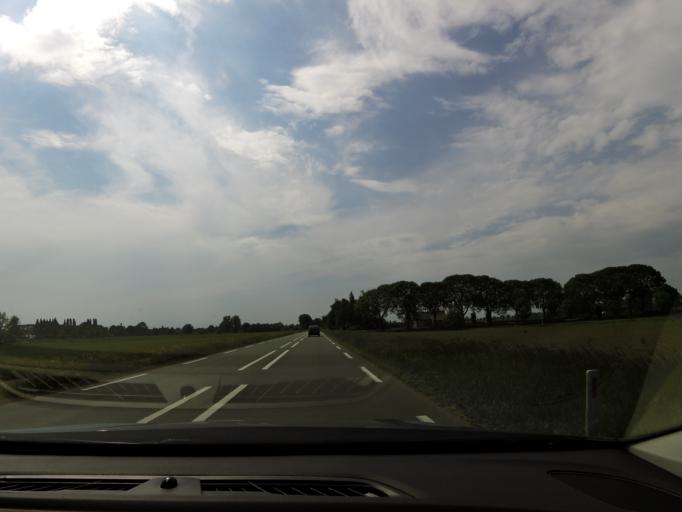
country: NL
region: North Brabant
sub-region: Gemeente Woudrichem
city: Almkerk
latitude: 51.7758
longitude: 4.9764
